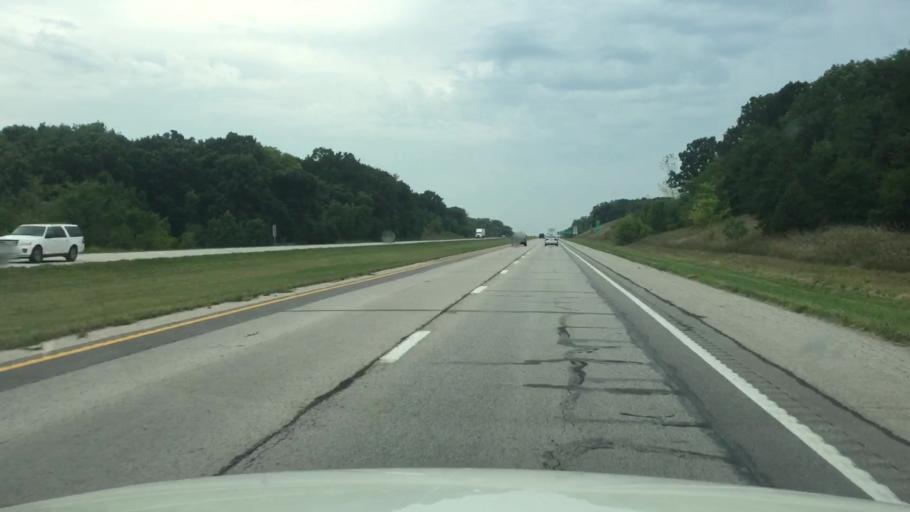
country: US
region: Missouri
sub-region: Harrison County
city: Bethany
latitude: 40.0992
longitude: -94.0769
